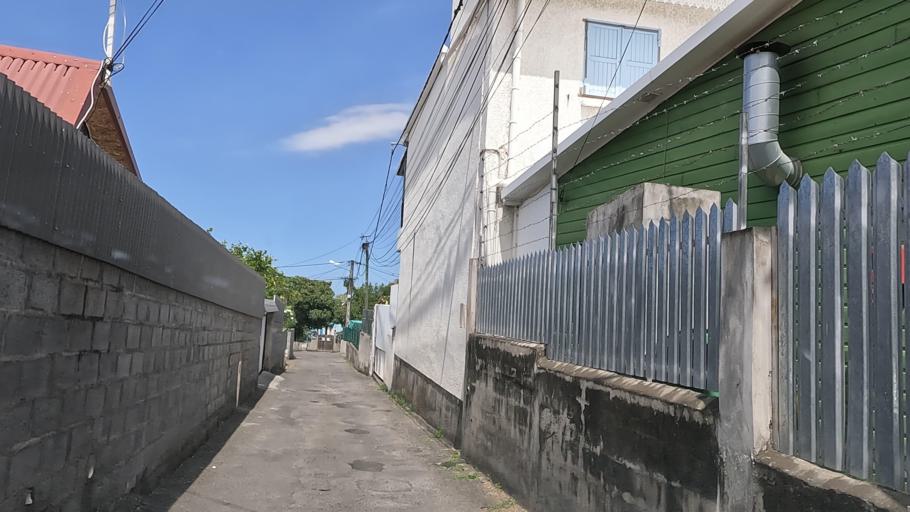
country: RE
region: Reunion
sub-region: Reunion
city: Saint-Louis
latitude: -21.2757
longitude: 55.4494
